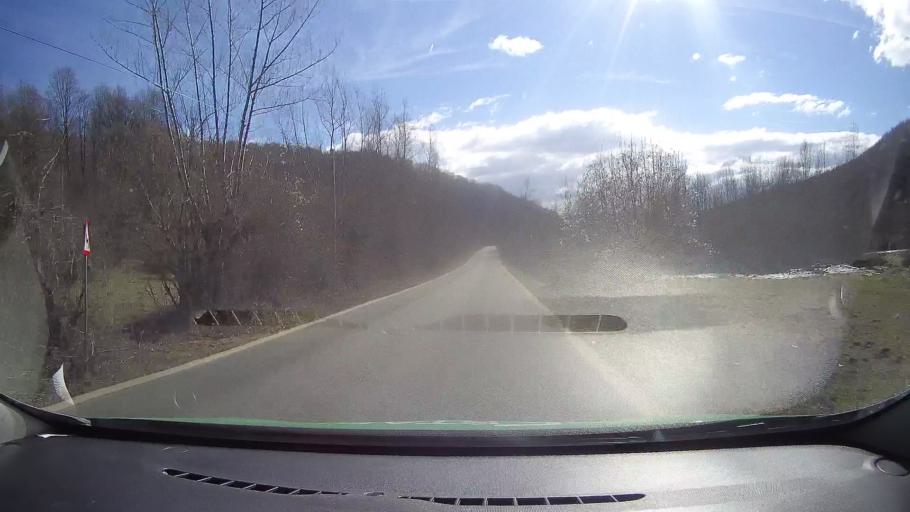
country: RO
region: Dambovita
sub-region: Comuna Vulcana-Pandele
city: Gura Vulcanei
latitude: 45.0482
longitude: 25.3873
